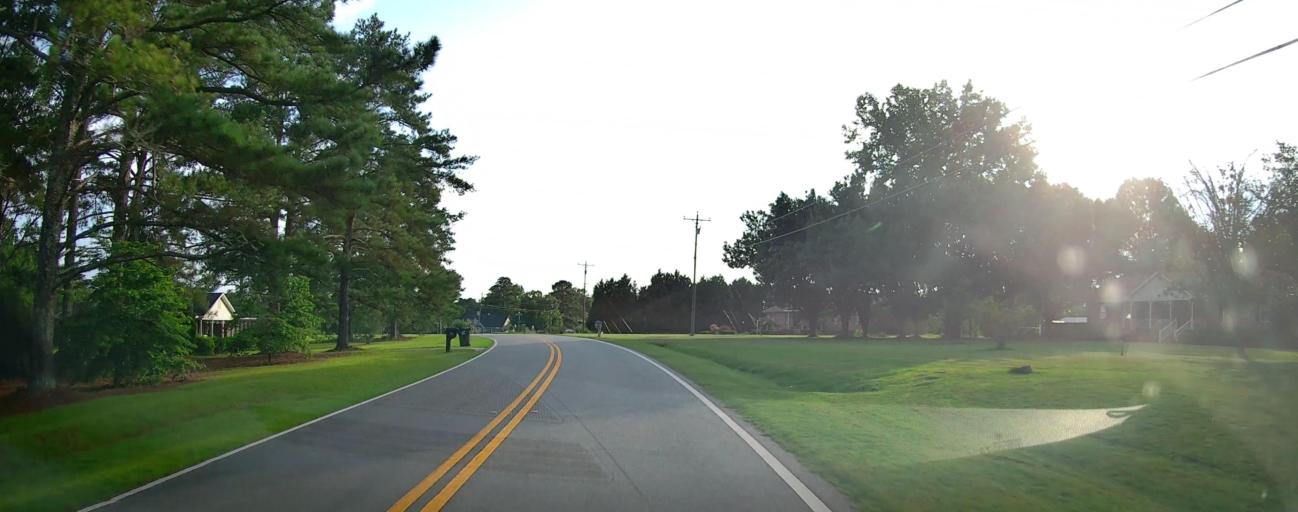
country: US
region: Georgia
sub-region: Peach County
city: Byron
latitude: 32.7345
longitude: -83.7380
